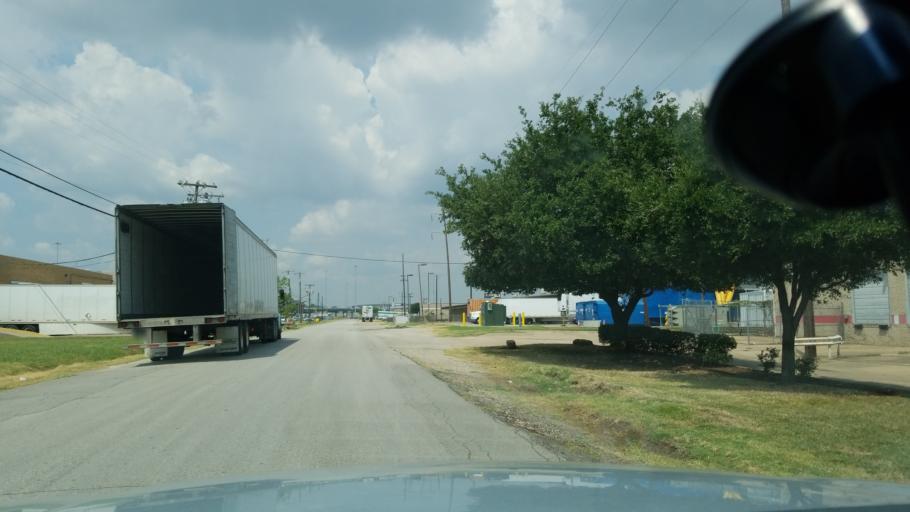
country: US
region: Texas
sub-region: Dallas County
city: Irving
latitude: 32.8368
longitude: -96.8956
